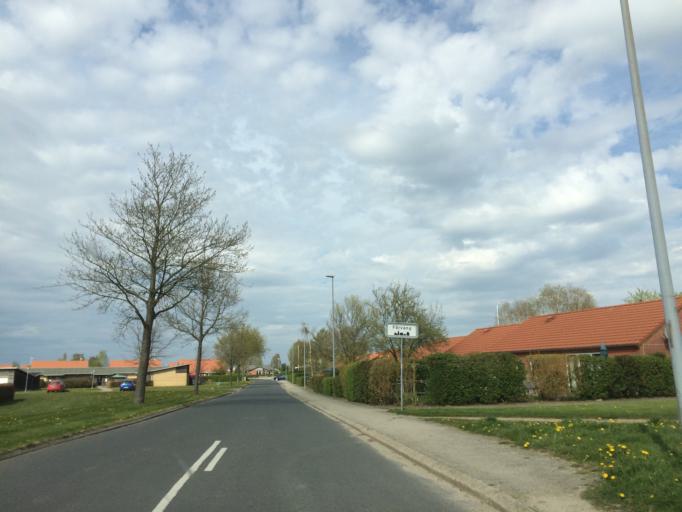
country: DK
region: Central Jutland
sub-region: Viborg Kommune
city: Bjerringbro
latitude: 56.2630
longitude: 9.7282
